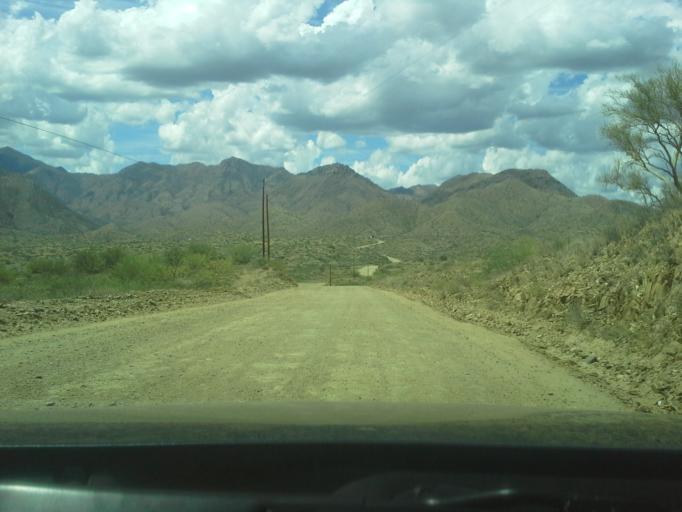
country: US
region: Arizona
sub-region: Yavapai County
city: Spring Valley
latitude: 34.2751
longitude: -112.2193
